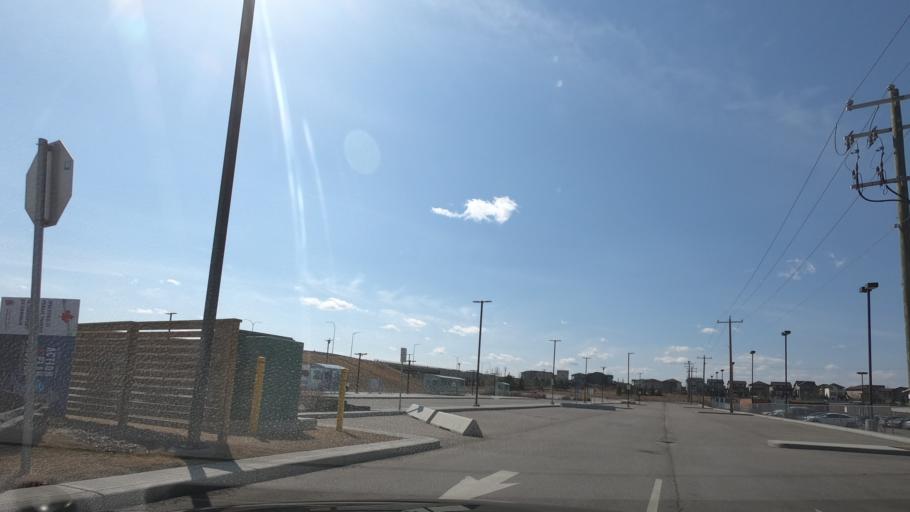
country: CA
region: Alberta
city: Airdrie
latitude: 51.2573
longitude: -114.0054
